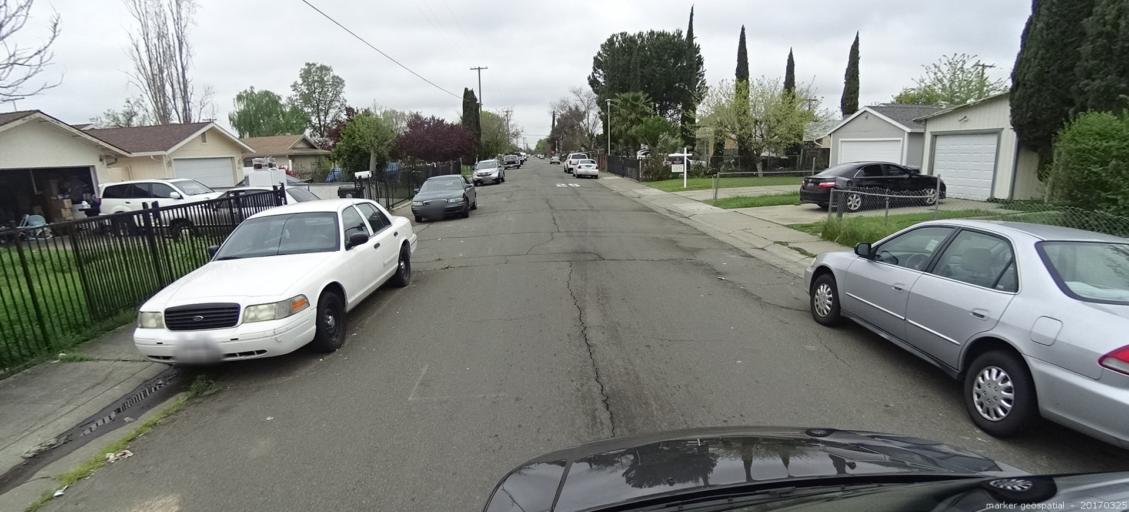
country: US
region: California
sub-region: Sacramento County
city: Florin
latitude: 38.5189
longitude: -121.4096
